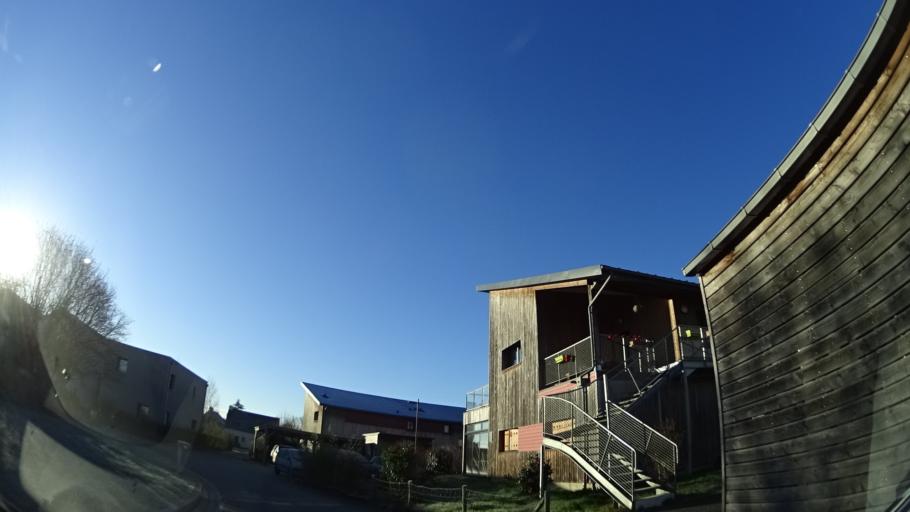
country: FR
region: Brittany
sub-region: Departement d'Ille-et-Vilaine
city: Chevaigne
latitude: 48.2076
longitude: -1.6267
